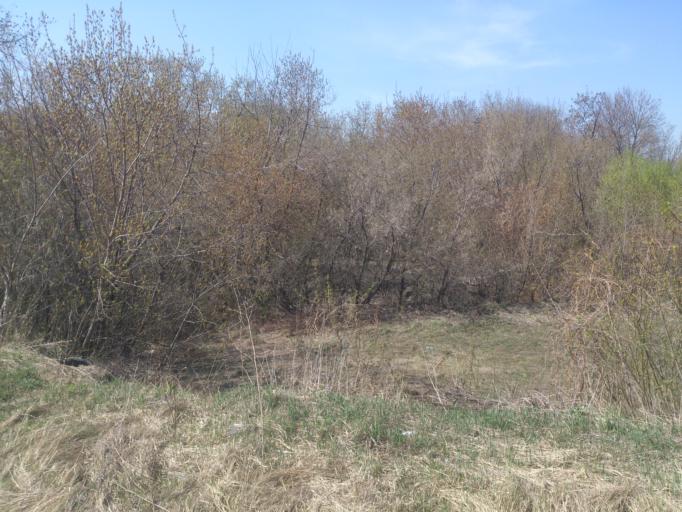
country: RU
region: Ulyanovsk
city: Novoul'yanovsk
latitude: 54.2155
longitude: 48.3055
